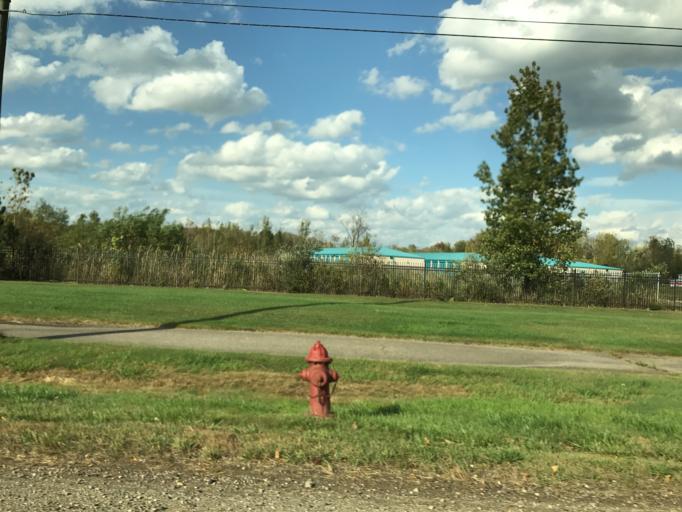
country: US
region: Michigan
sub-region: Oakland County
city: Wixom
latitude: 42.5002
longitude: -83.5624
